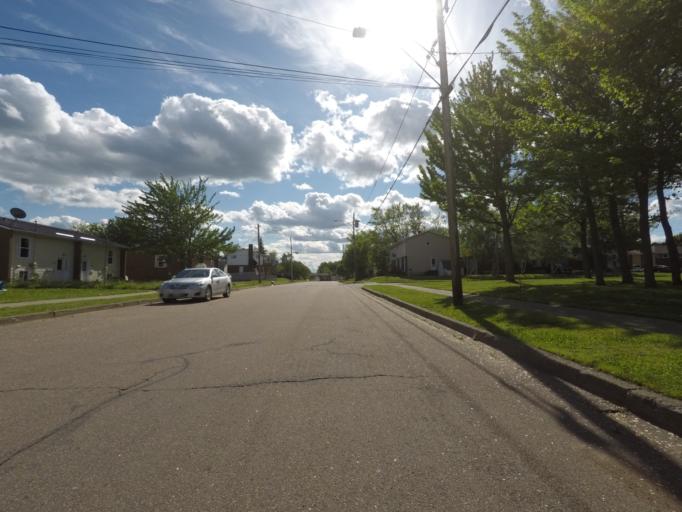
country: CA
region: New Brunswick
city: Moncton
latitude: 46.0992
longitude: -64.8243
